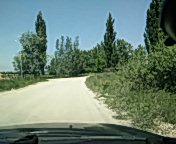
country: HU
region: Fejer
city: Bicske
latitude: 47.4700
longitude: 18.5824
